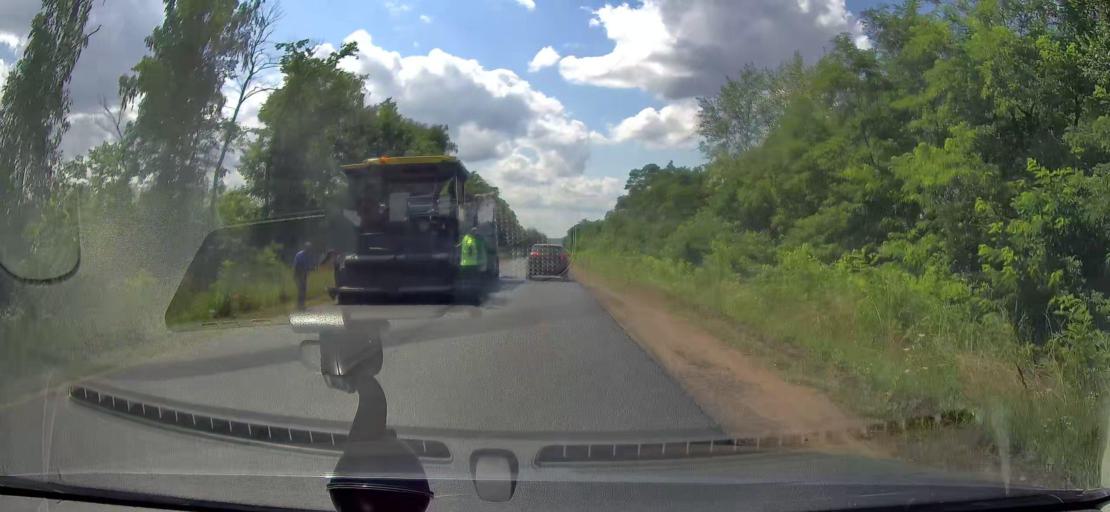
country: RU
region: Kursk
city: Zolotukhino
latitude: 51.9700
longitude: 36.2891
